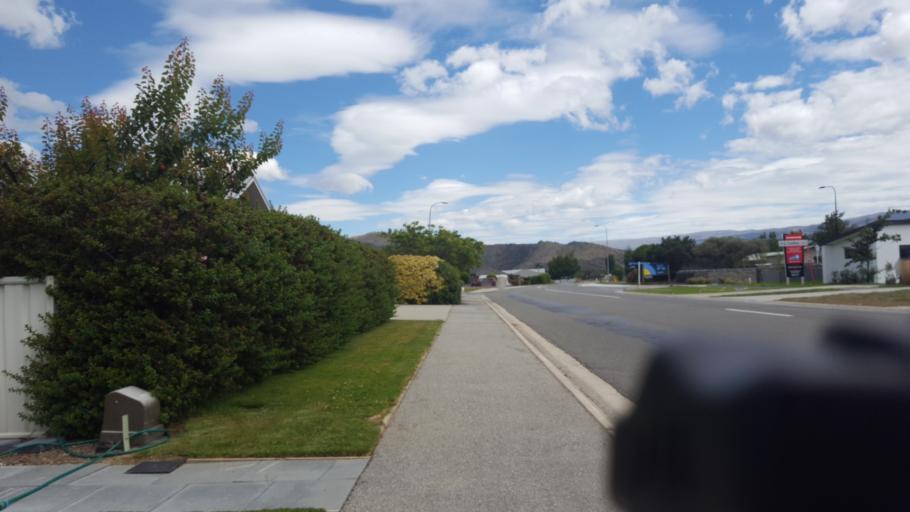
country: NZ
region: Otago
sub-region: Queenstown-Lakes District
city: Wanaka
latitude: -45.0384
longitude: 169.2159
